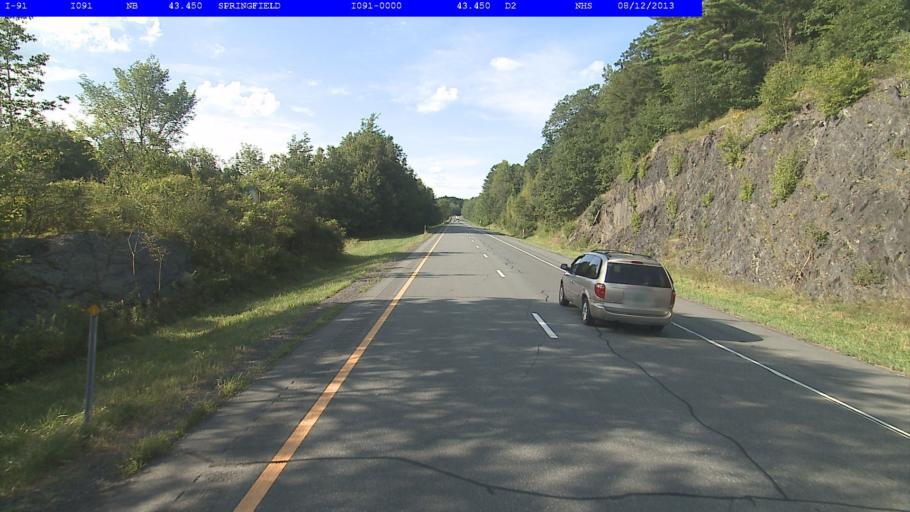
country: US
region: New Hampshire
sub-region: Sullivan County
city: Charlestown
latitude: 43.2906
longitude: -72.4272
